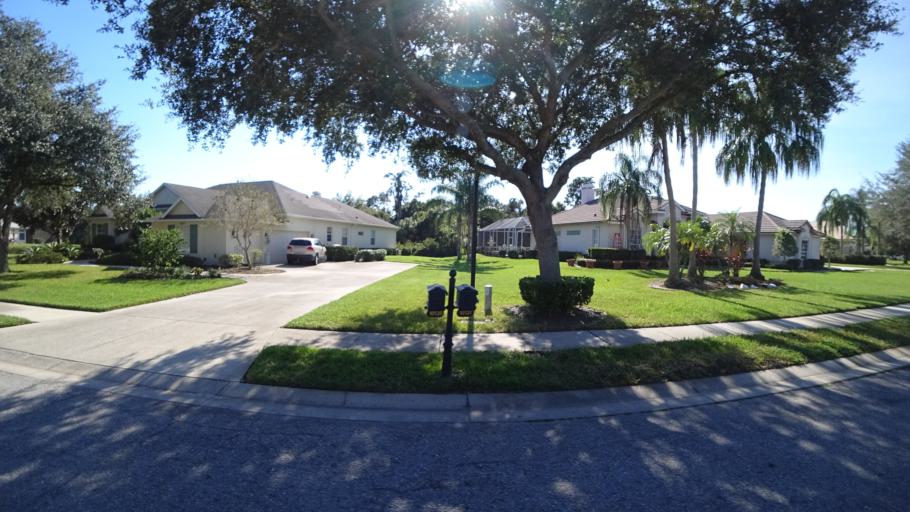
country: US
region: Florida
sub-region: Sarasota County
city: The Meadows
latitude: 27.4049
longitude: -82.4392
